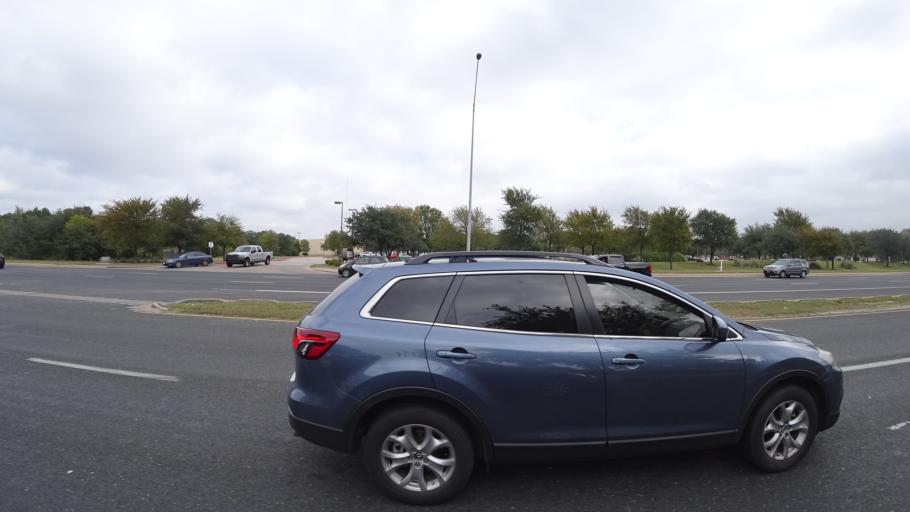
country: US
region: Texas
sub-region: Travis County
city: Shady Hollow
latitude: 30.2145
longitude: -97.8320
